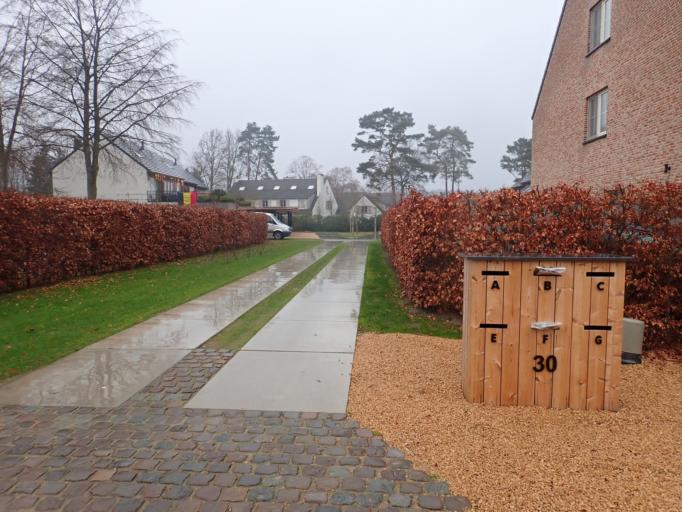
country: BE
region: Flanders
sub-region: Provincie Antwerpen
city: Zandhoven
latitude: 51.2392
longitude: 4.6410
